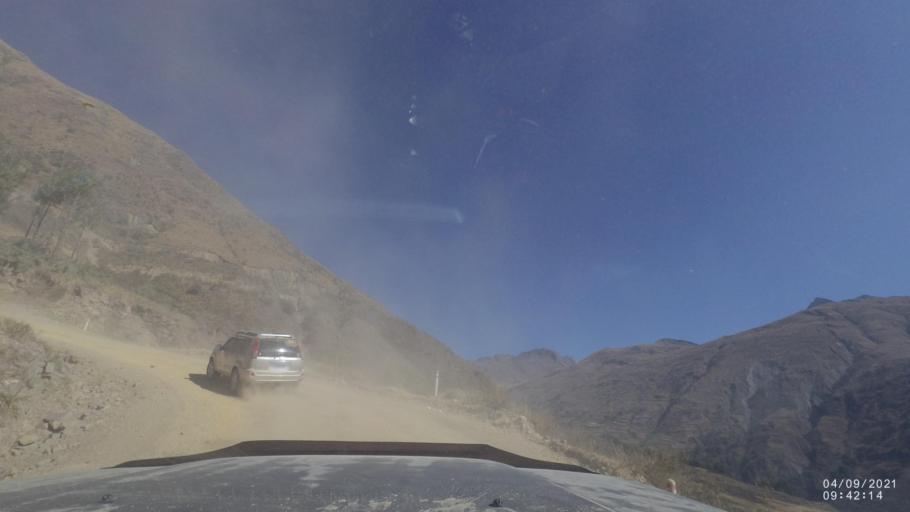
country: BO
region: Cochabamba
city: Sipe Sipe
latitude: -17.3393
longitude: -66.3892
